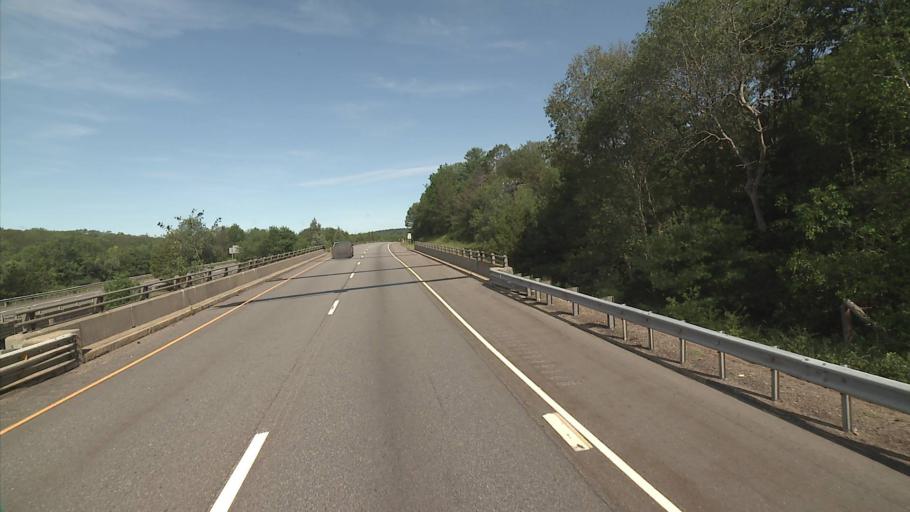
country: US
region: Connecticut
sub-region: New London County
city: Colchester
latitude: 41.5738
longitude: -72.3450
